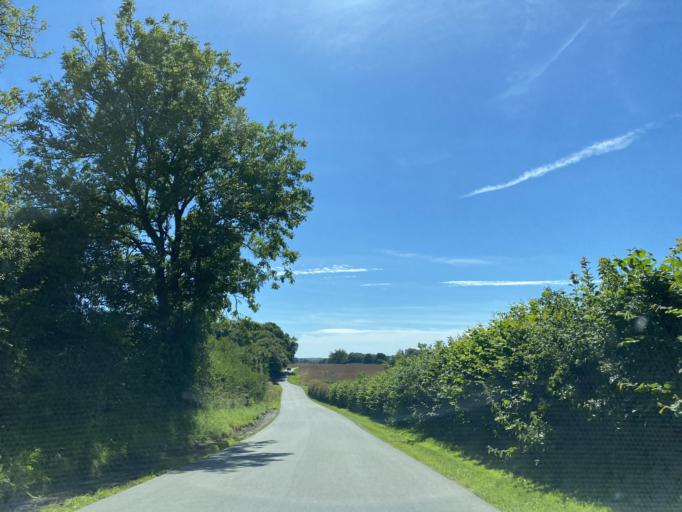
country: DK
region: South Denmark
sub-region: Kolding Kommune
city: Christiansfeld
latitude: 55.3871
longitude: 9.5151
